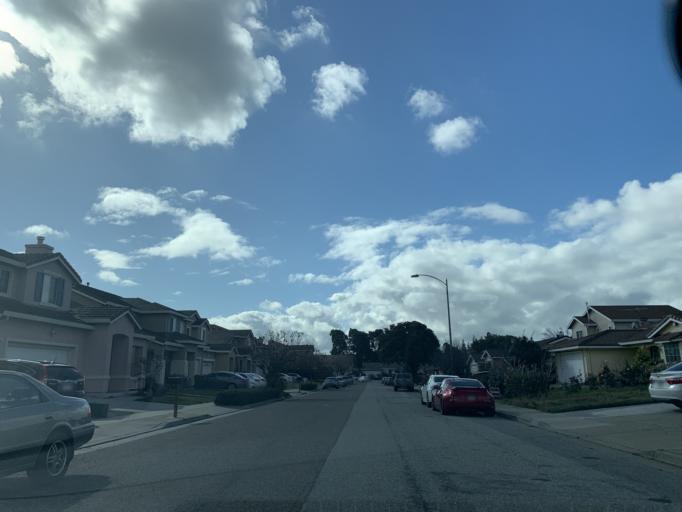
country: US
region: California
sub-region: Santa Clara County
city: Alum Rock
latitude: 37.3929
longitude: -121.8686
